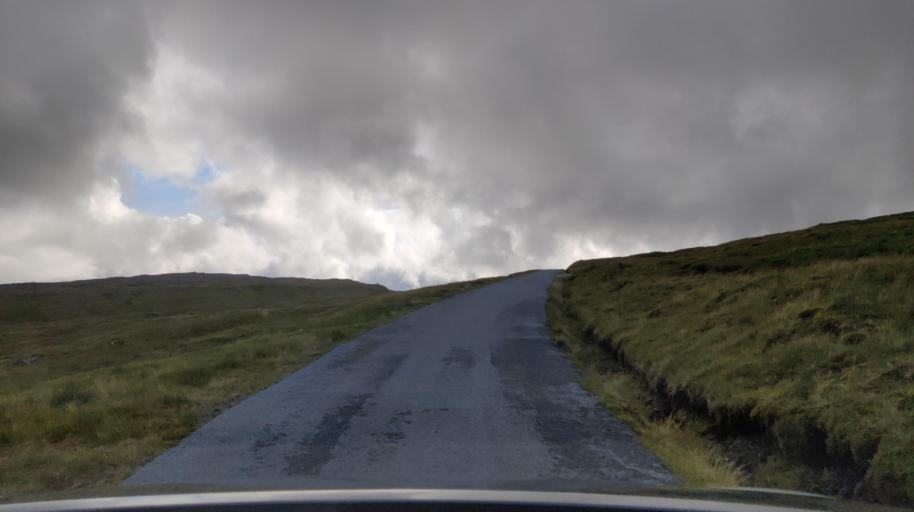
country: FO
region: Streymoy
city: Vestmanna
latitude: 62.1730
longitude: -7.1567
